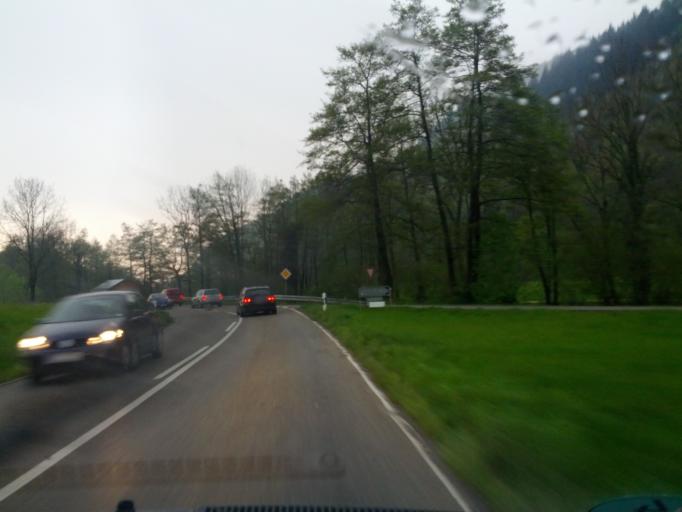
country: DE
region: Baden-Wuerttemberg
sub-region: Freiburg Region
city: Muenstertal/Schwarzwald
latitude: 47.8662
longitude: 7.7481
